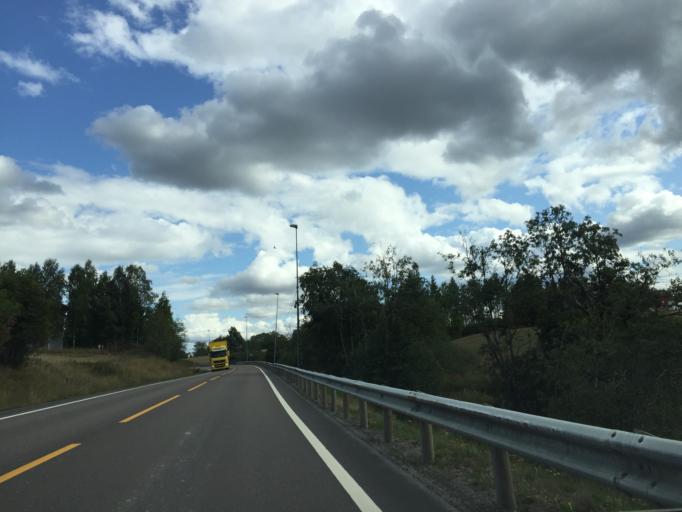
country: NO
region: Ostfold
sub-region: Hobol
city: Elvestad
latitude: 59.6229
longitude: 10.9803
